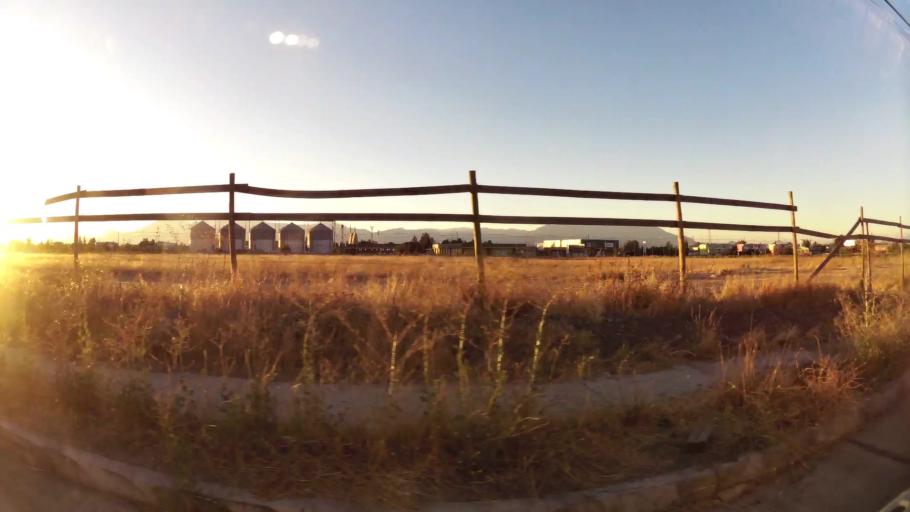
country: CL
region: O'Higgins
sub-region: Provincia de Cachapoal
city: Rancagua
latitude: -34.1873
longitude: -70.7403
